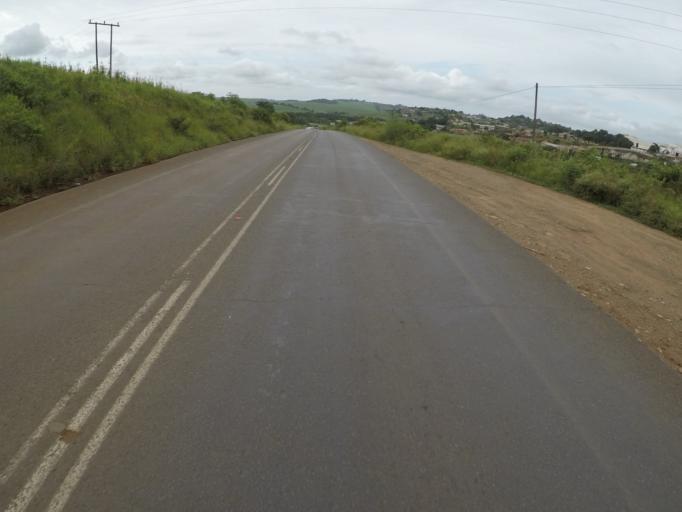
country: ZA
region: KwaZulu-Natal
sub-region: uThungulu District Municipality
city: Empangeni
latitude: -28.7731
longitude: 31.8756
